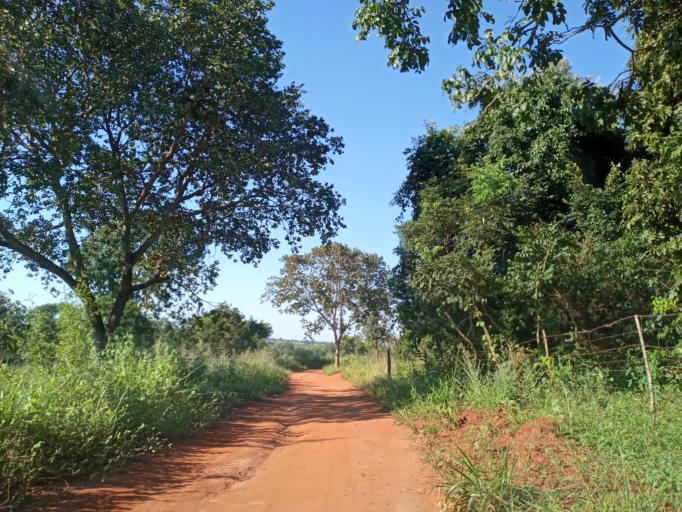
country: BR
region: Minas Gerais
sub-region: Ituiutaba
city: Ituiutaba
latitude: -18.9748
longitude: -49.4978
